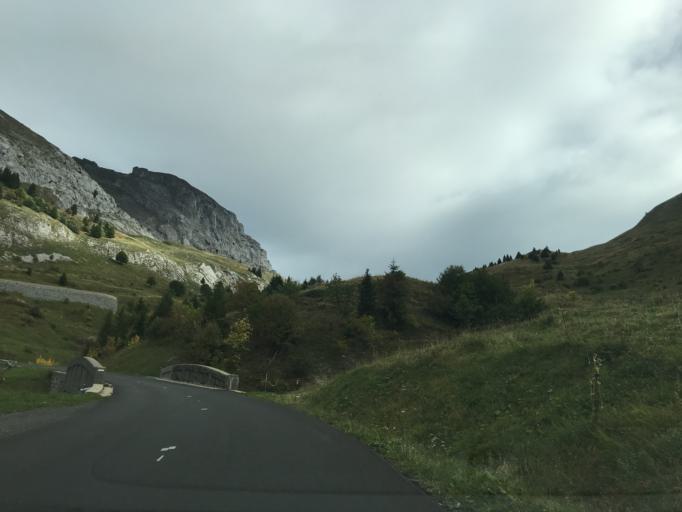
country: FR
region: Rhone-Alpes
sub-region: Departement de la Haute-Savoie
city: Le Grand-Bornand
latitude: 45.9876
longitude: 6.4708
